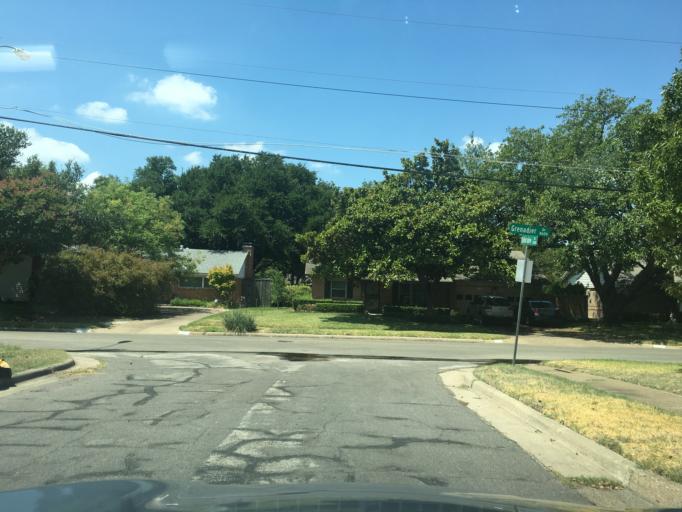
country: US
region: Texas
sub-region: Dallas County
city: Garland
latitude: 32.8663
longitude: -96.6905
